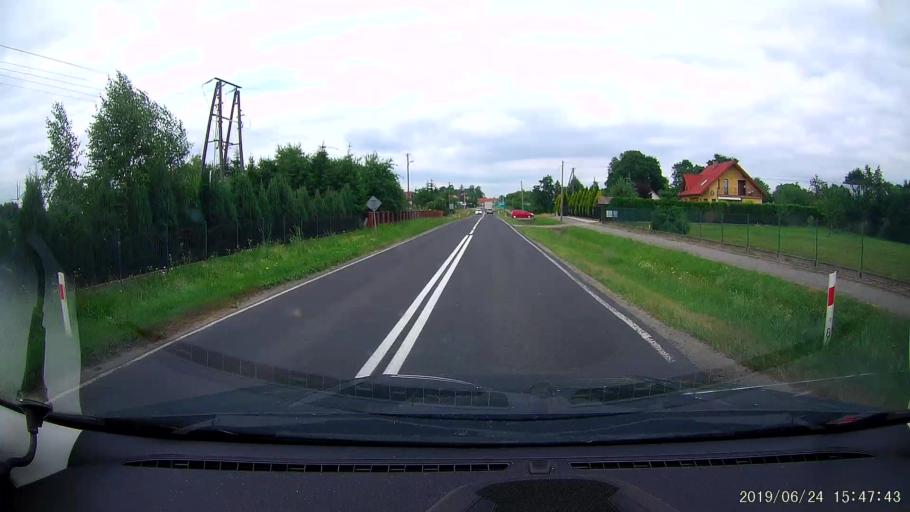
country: PL
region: Subcarpathian Voivodeship
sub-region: Powiat lubaczowski
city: Oleszyce
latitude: 50.1659
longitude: 23.0233
